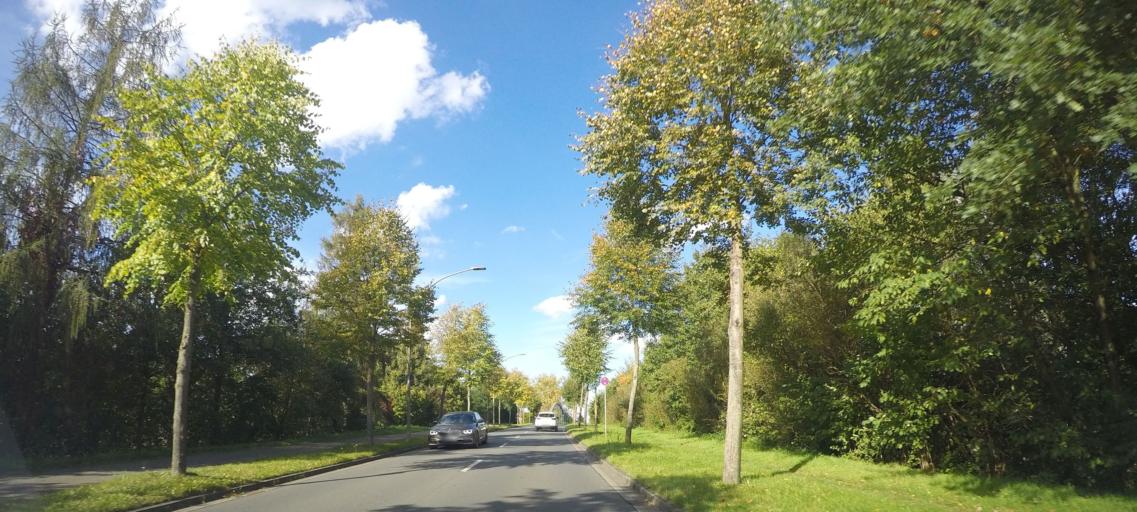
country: DE
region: North Rhine-Westphalia
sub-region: Regierungsbezirk Arnsberg
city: Hamm
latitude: 51.6927
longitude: 7.8825
